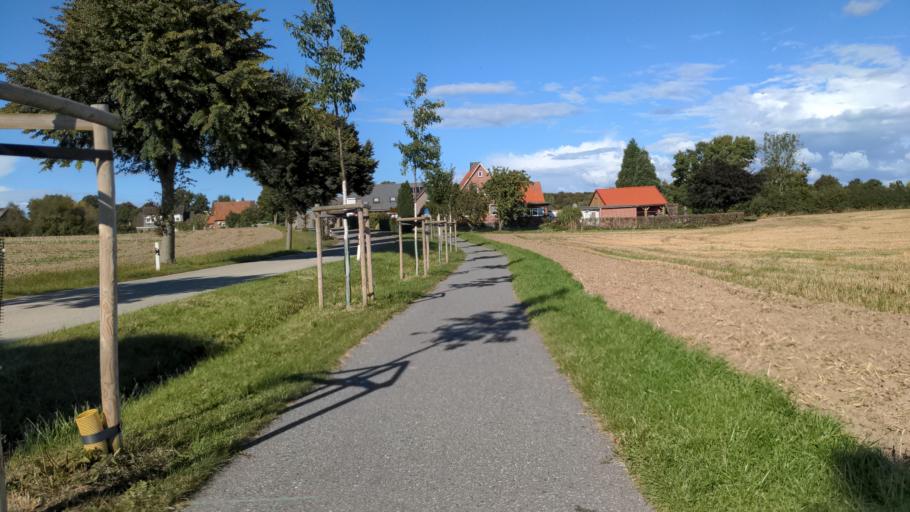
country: DE
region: Schleswig-Holstein
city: Gromitz
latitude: 54.1706
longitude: 10.9390
